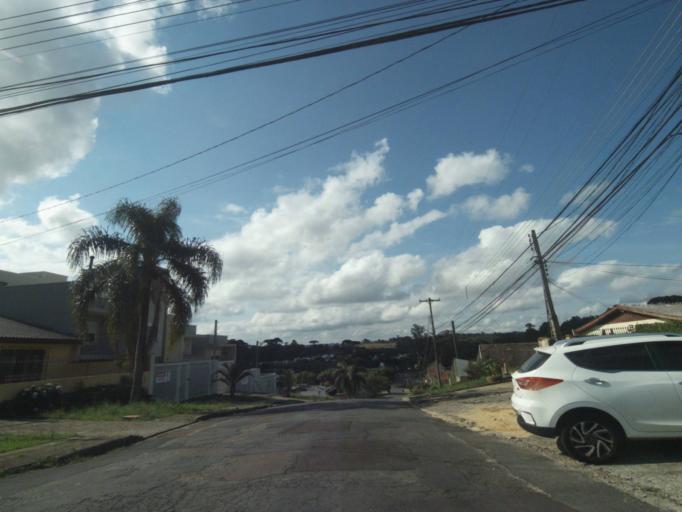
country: BR
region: Parana
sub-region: Curitiba
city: Curitiba
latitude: -25.3904
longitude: -49.3010
